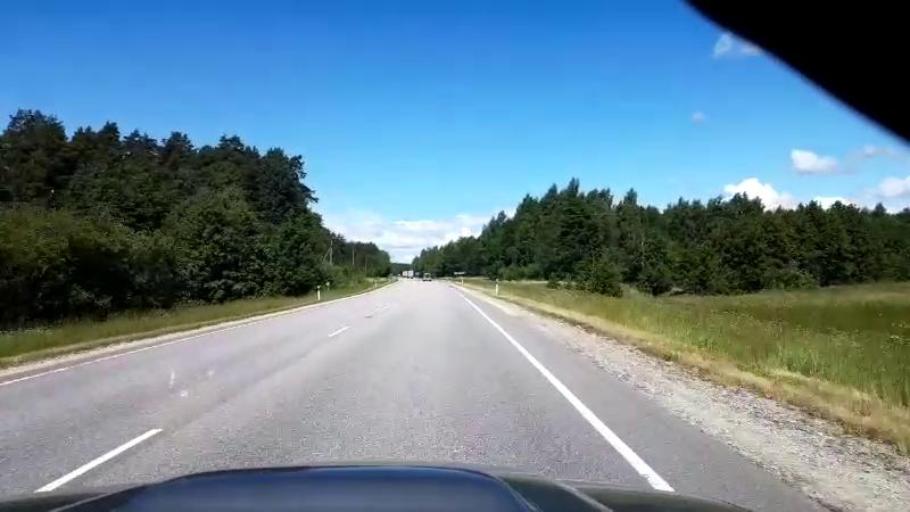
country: LV
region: Salacgrivas
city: Ainazi
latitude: 58.0822
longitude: 24.5102
